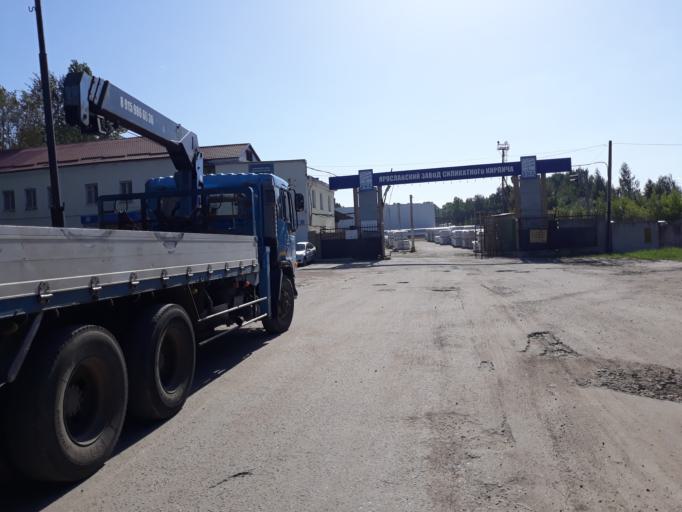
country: RU
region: Jaroslavl
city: Yaroslavl
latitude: 57.5959
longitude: 39.8549
